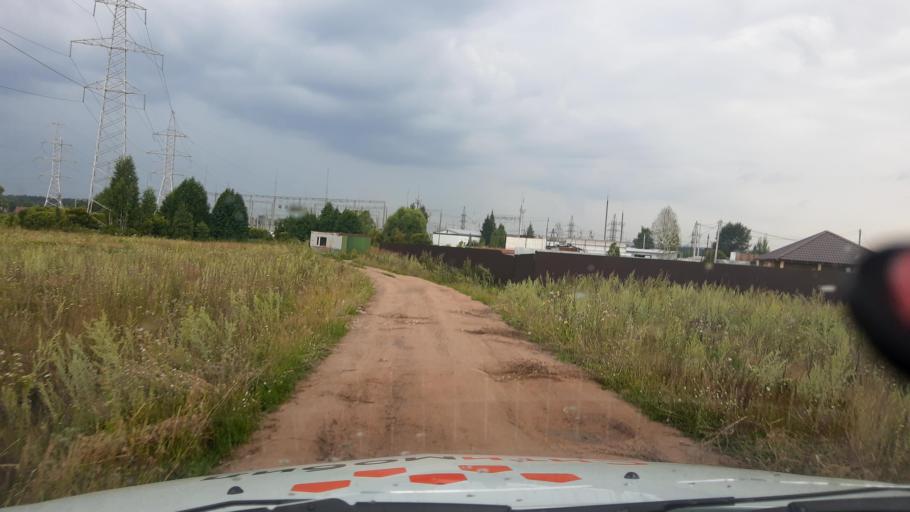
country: RU
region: Bashkortostan
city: Ufa
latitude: 54.6722
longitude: 56.0889
